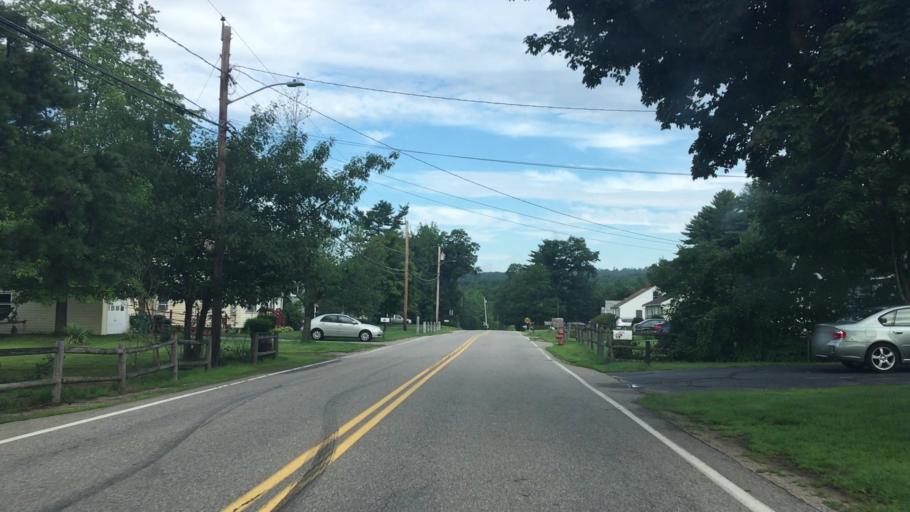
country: US
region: New Hampshire
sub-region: Strafford County
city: Rochester
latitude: 43.3492
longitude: -70.9776
